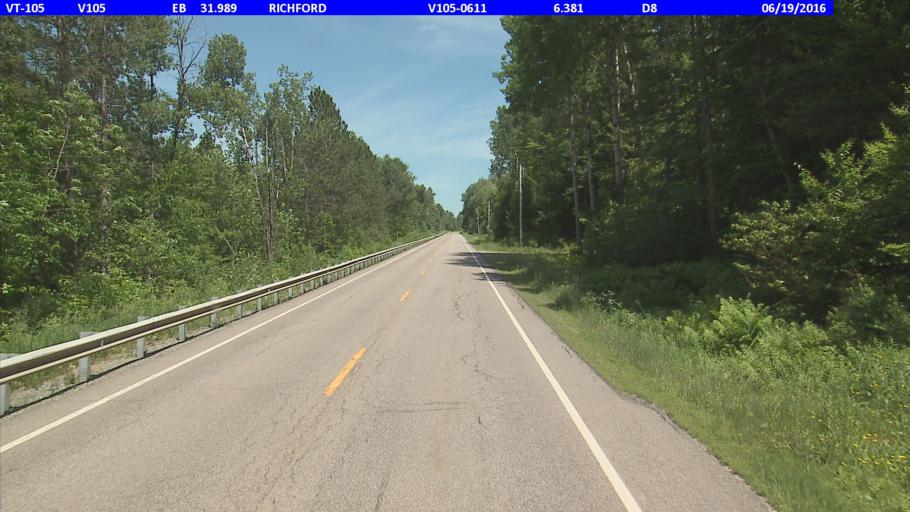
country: US
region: Vermont
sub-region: Franklin County
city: Richford
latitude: 45.0017
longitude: -72.5948
